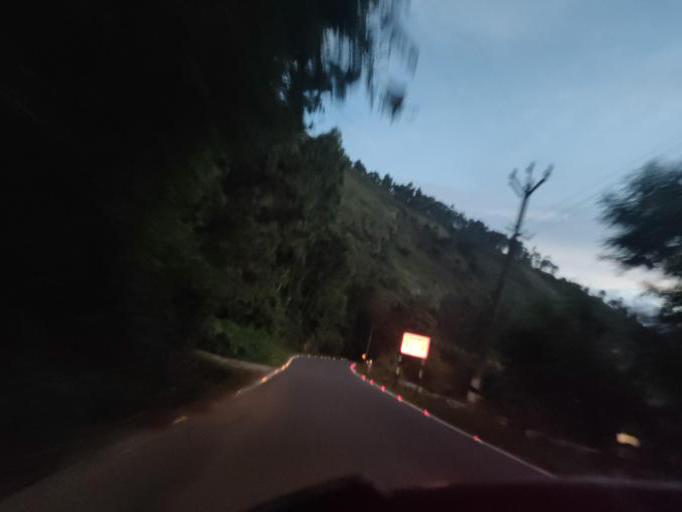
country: IN
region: Tamil Nadu
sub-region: Dindigul
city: Kodaikanal
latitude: 10.2861
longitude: 77.5395
